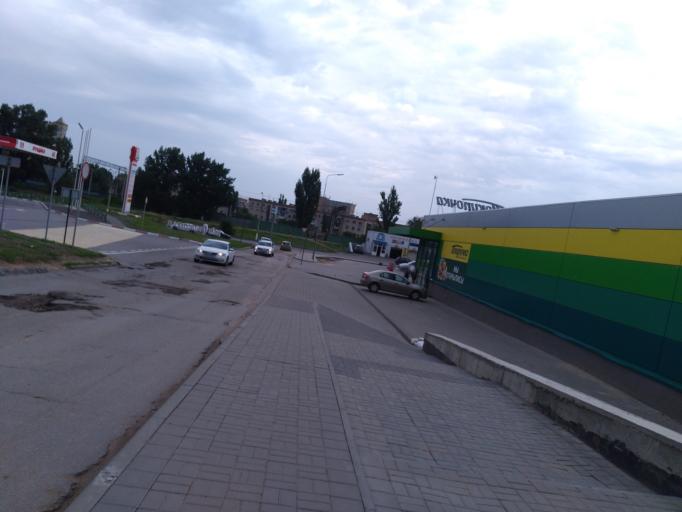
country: RU
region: Volgograd
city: Volgograd
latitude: 48.7233
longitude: 44.5258
